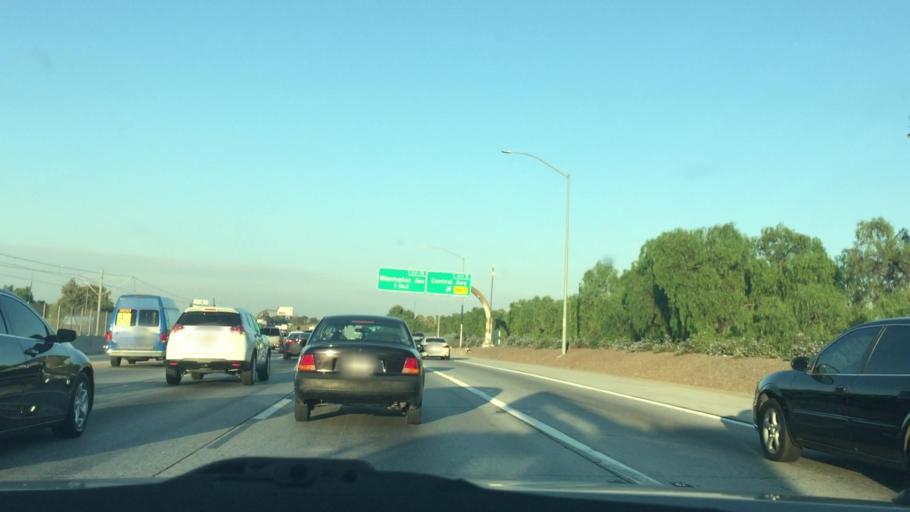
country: US
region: California
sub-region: Los Angeles County
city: Willowbrook
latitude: 33.9273
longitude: -118.2600
